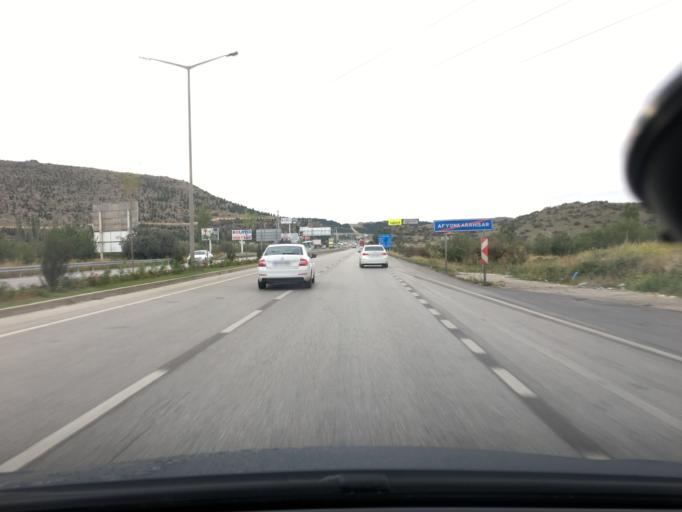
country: TR
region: Afyonkarahisar
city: Afyonkarahisar
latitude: 38.7919
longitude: 30.4516
